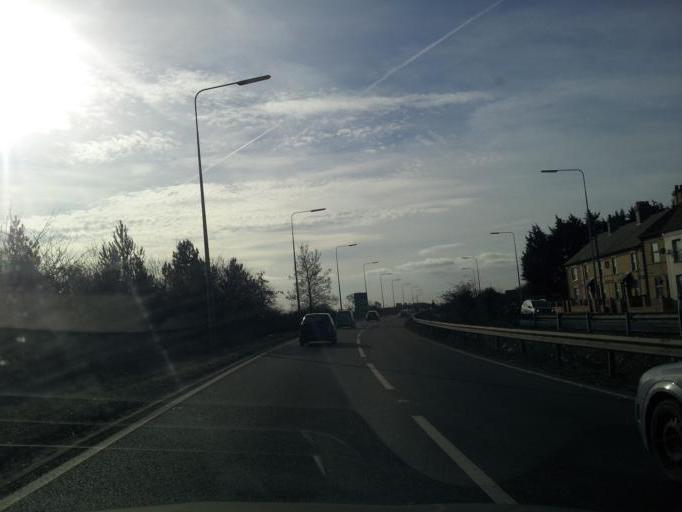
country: GB
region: England
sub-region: Central Bedfordshire
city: Biggleswade
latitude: 52.1043
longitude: -0.2773
